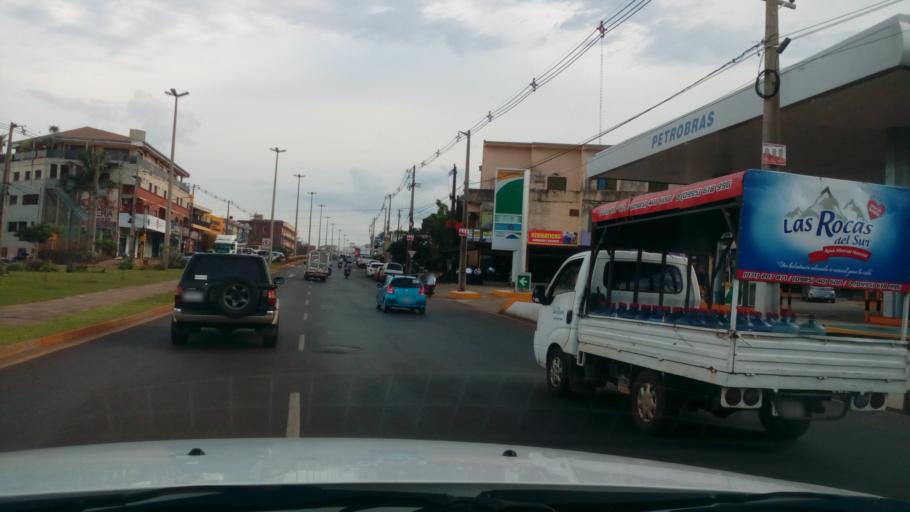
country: PY
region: Itapua
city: Encarnacion
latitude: -27.3484
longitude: -55.8584
